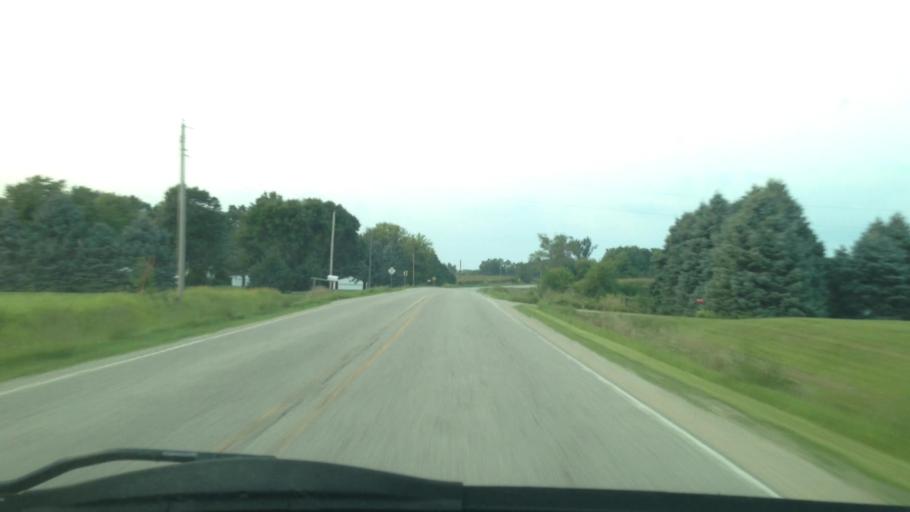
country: US
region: Iowa
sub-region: Benton County
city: Urbana
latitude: 42.1544
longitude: -91.8777
